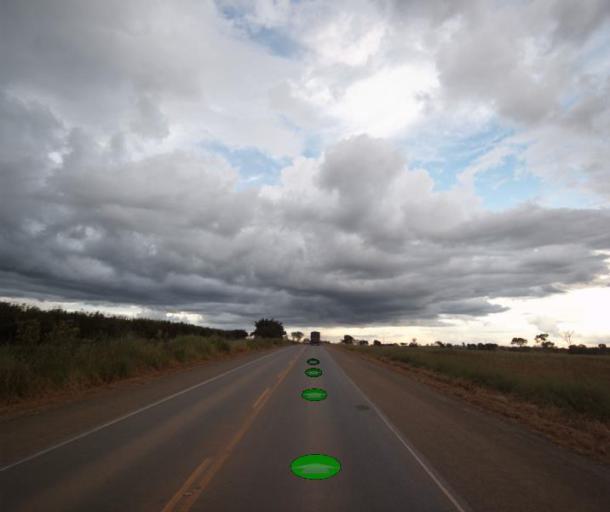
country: BR
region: Goias
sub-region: Uruacu
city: Uruacu
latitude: -14.7539
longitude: -49.2553
